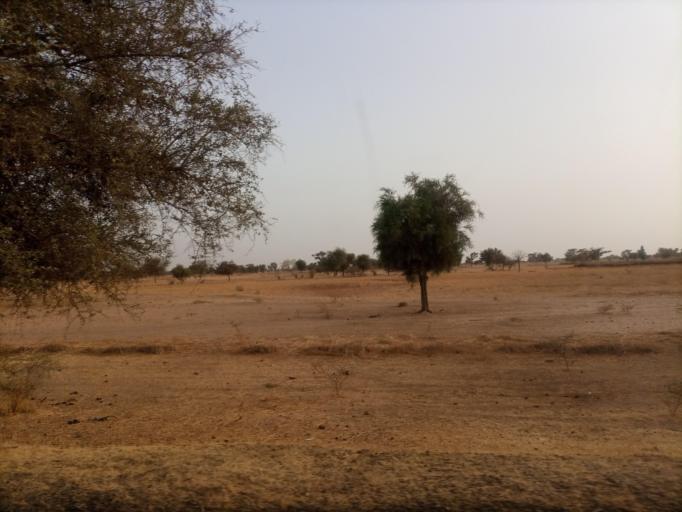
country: SN
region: Louga
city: Louga
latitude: 15.5309
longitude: -16.0781
